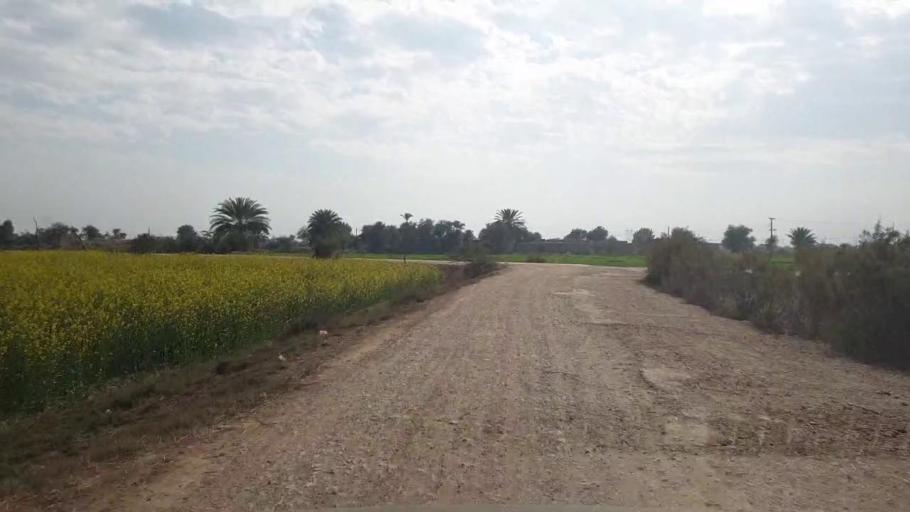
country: PK
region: Sindh
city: Sakrand
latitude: 26.0021
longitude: 68.4048
